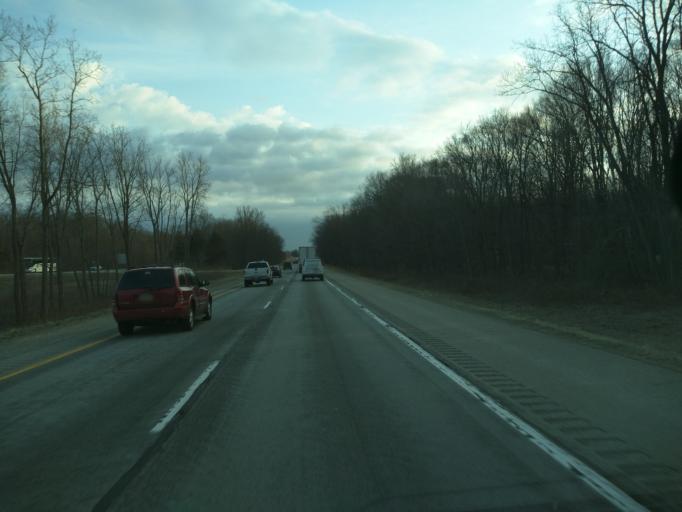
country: US
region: Michigan
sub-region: Ingham County
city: Holt
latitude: 42.6528
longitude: -84.4766
